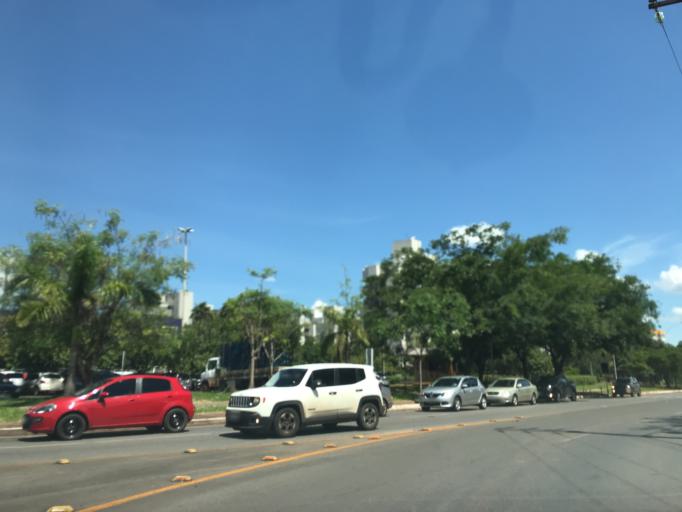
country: BR
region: Federal District
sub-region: Brasilia
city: Brasilia
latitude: -15.8004
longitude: -47.9244
